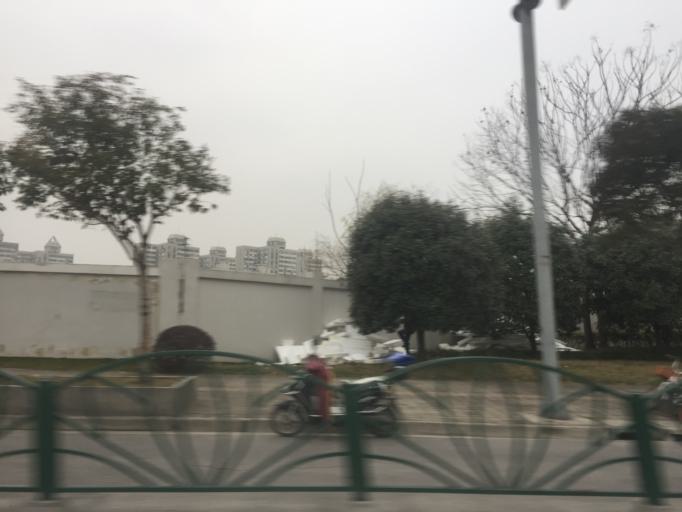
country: CN
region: Shanghai Shi
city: Luwan
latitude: 31.1876
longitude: 121.4970
